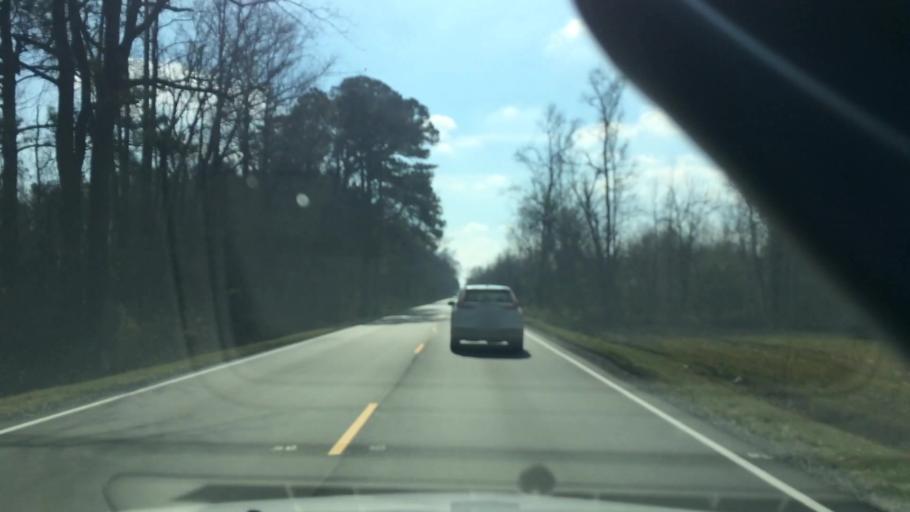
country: US
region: North Carolina
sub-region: Duplin County
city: Beulaville
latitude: 34.9527
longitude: -77.7666
